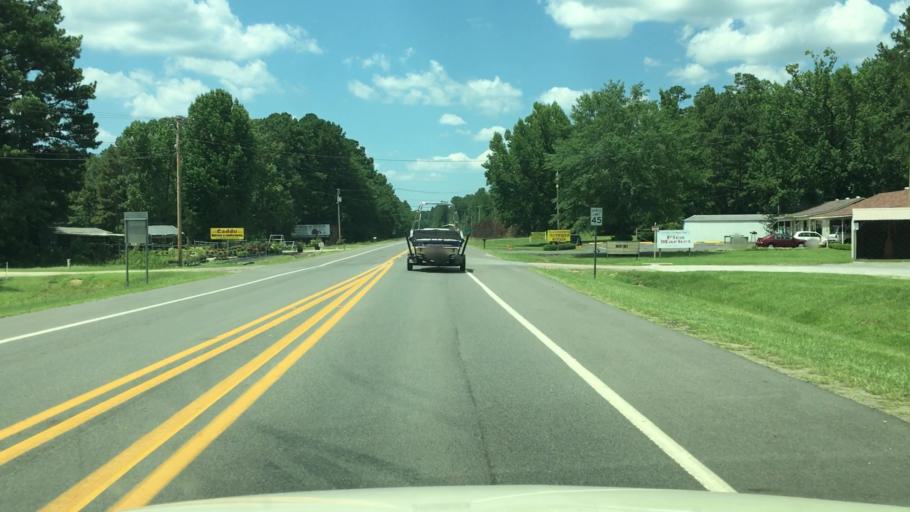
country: US
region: Arkansas
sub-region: Clark County
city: Arkadelphia
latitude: 34.1894
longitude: -93.0724
